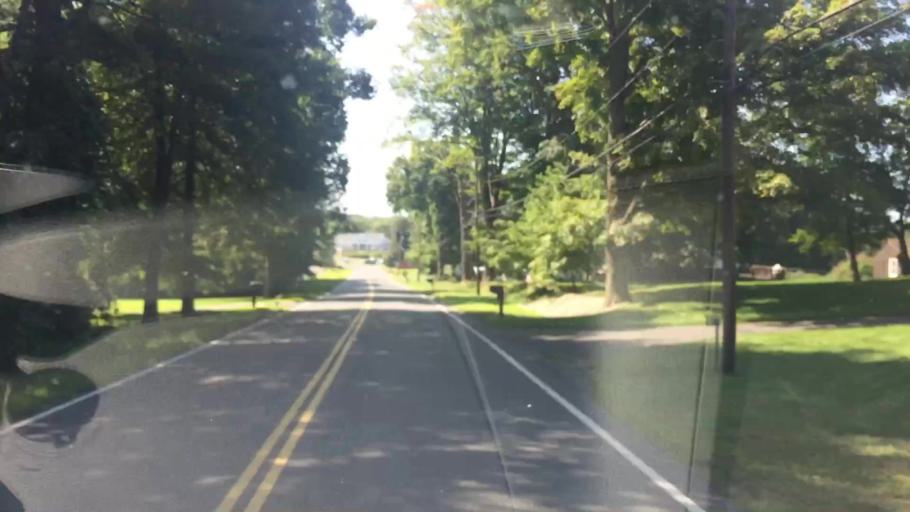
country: US
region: Massachusetts
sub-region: Hampshire County
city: Granby
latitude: 42.2523
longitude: -72.5423
